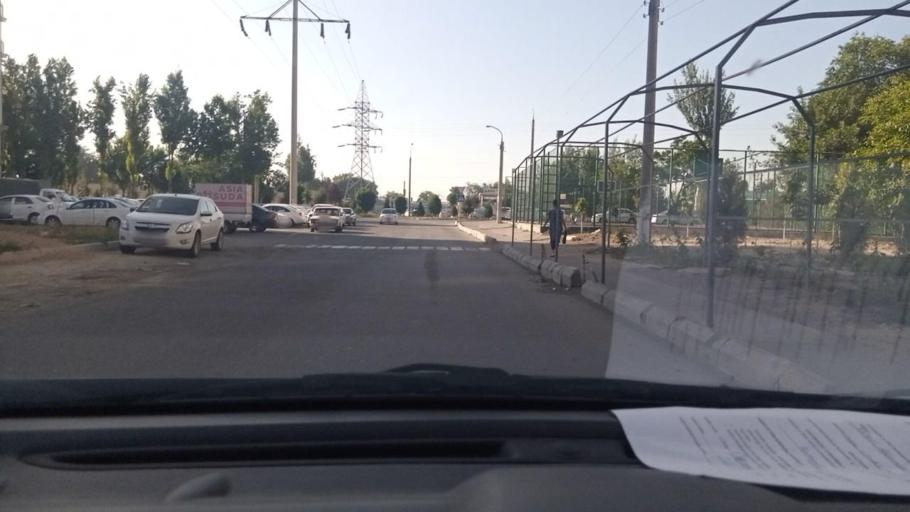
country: UZ
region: Toshkent
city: Salor
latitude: 41.3216
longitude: 69.3605
